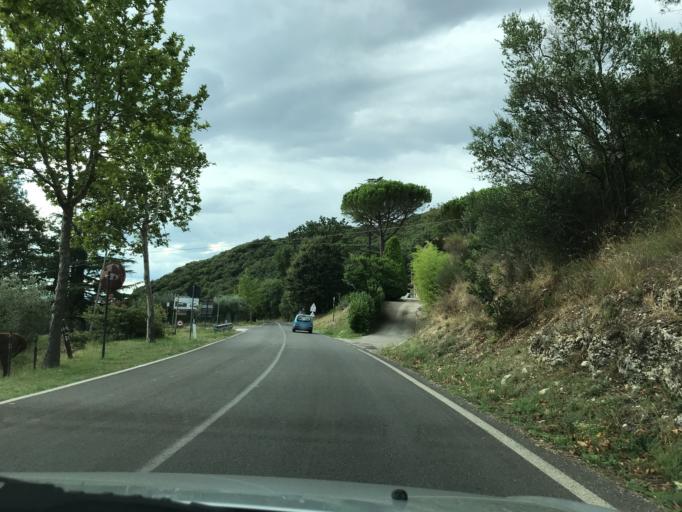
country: IT
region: Umbria
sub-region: Provincia di Terni
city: Guardea
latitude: 42.6303
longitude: 12.2964
